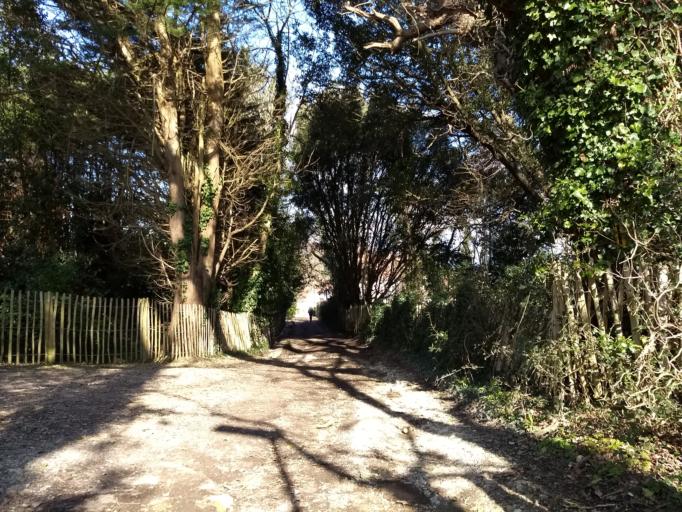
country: GB
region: England
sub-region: Isle of Wight
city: Seaview
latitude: 50.7121
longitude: -1.1064
